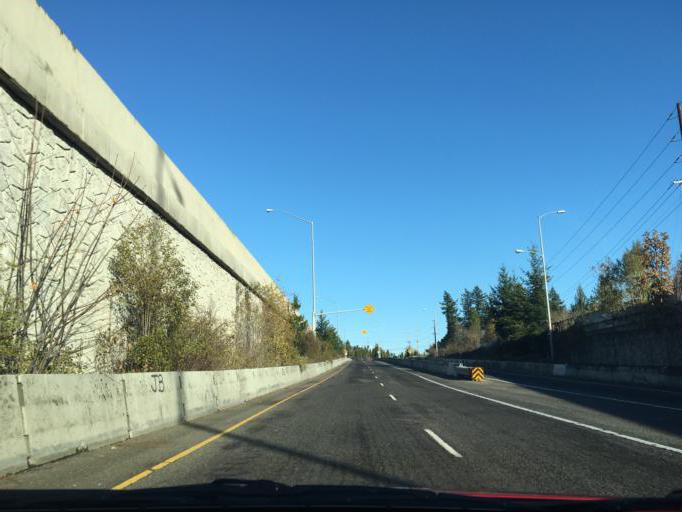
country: US
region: Oregon
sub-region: Washington County
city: West Slope
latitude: 45.5074
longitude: -122.7447
